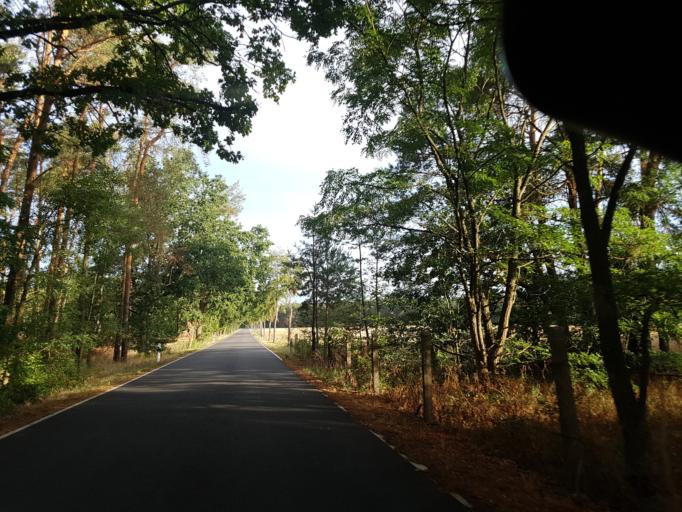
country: DE
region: Saxony-Anhalt
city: Holzdorf
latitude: 51.7893
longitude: 13.1084
